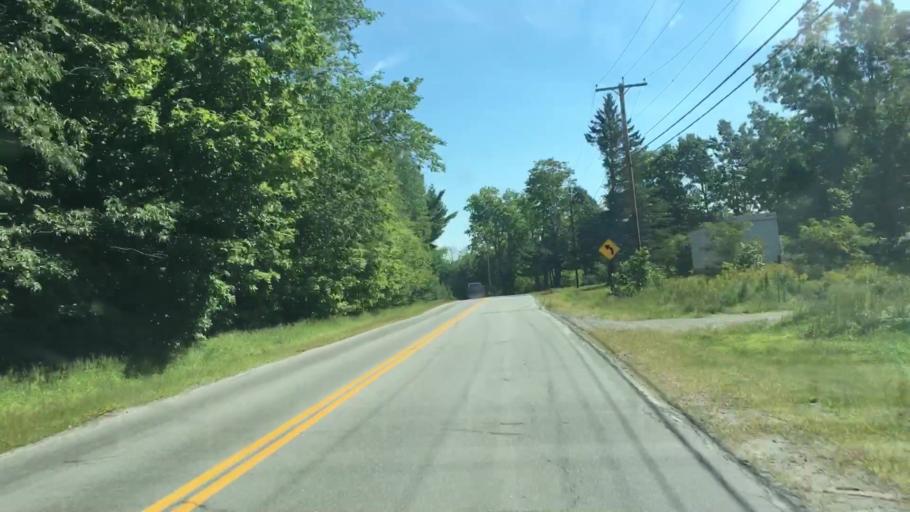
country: US
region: Maine
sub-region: Penobscot County
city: Bradford
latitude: 45.1713
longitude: -68.8500
